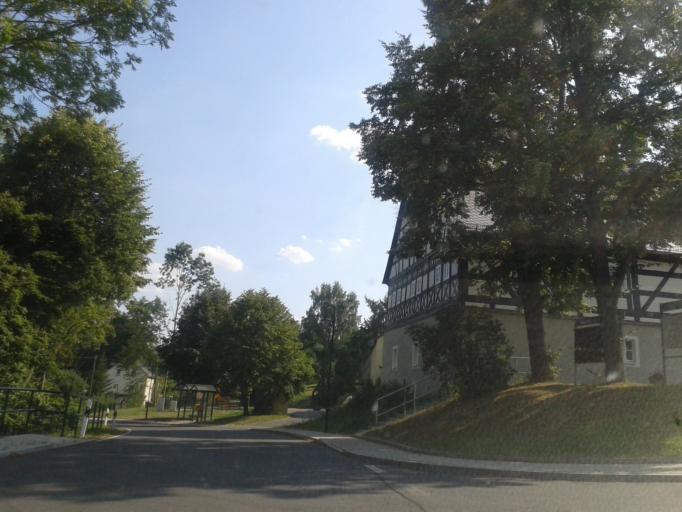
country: DE
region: Saxony
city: Niederschona
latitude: 50.9801
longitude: 13.4084
